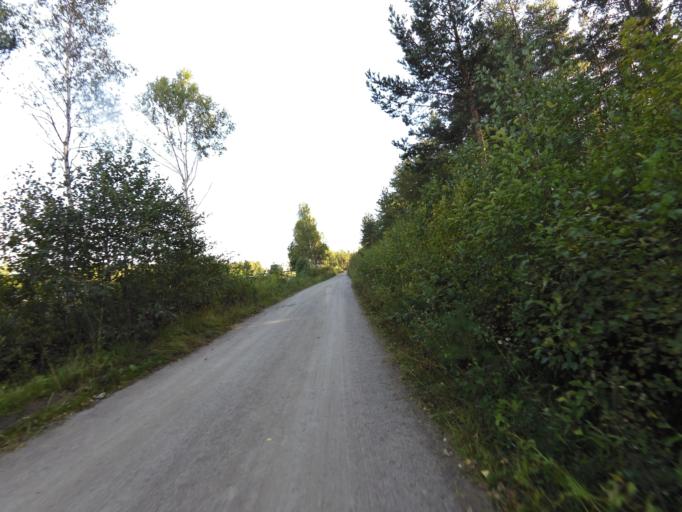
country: SE
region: Gaevleborg
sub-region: Gavle Kommun
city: Gavle
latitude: 60.6537
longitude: 17.1144
